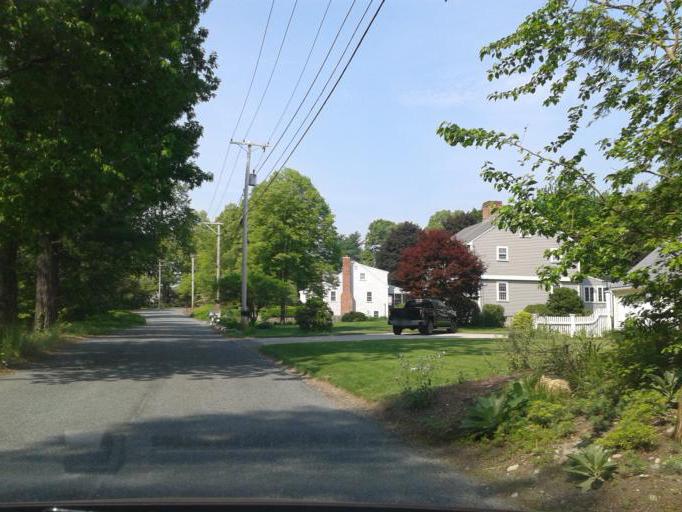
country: US
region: Massachusetts
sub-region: Worcester County
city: Westborough
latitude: 42.2426
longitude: -71.6106
